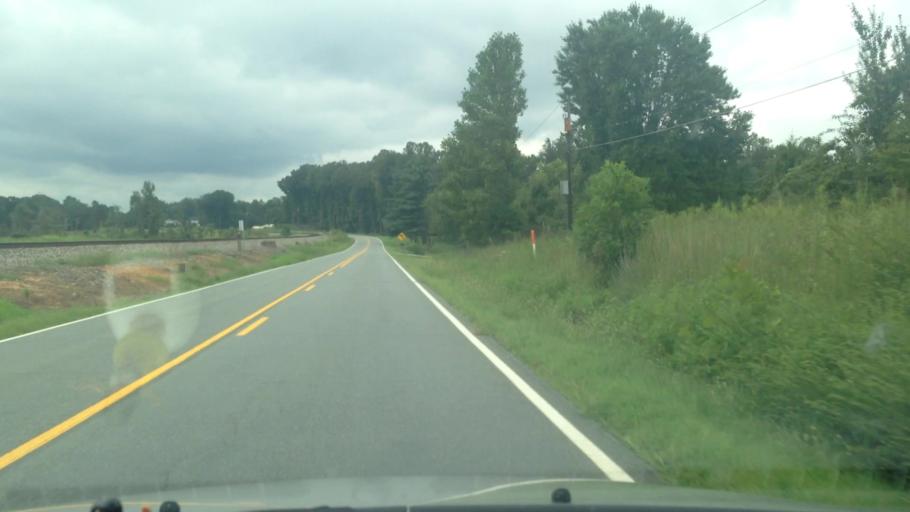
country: US
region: North Carolina
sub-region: Stokes County
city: Walnut Cove
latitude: 36.2493
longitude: -80.1516
